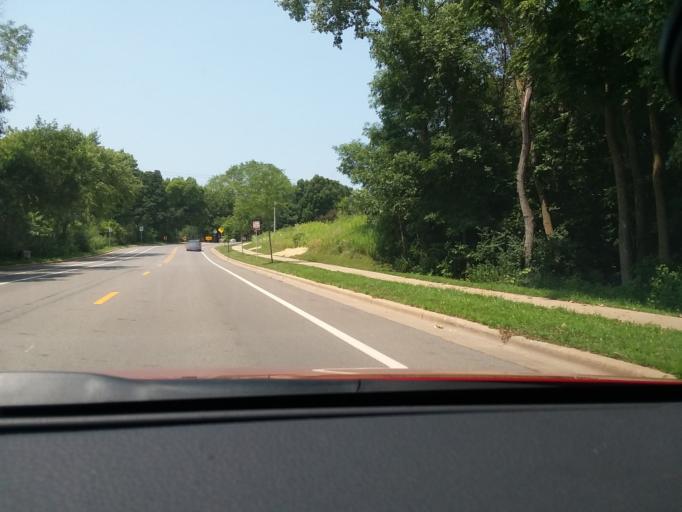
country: US
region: Wisconsin
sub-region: Dane County
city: Monona
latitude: 43.1138
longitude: -89.3135
